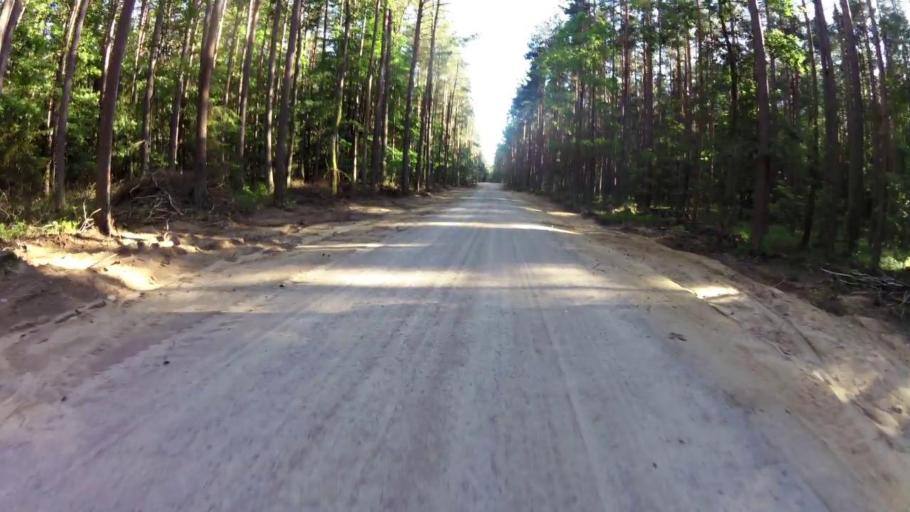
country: PL
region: West Pomeranian Voivodeship
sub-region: Powiat bialogardzki
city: Bialogard
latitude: 53.9639
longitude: 16.0989
